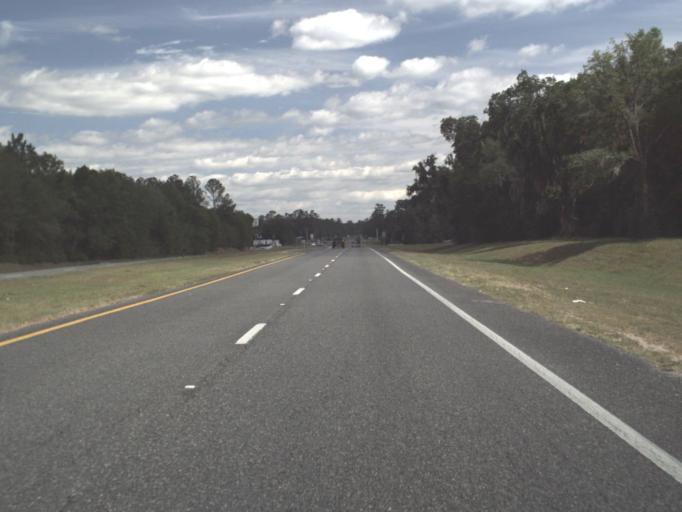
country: US
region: Florida
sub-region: Levy County
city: Williston
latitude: 29.2878
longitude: -82.3418
